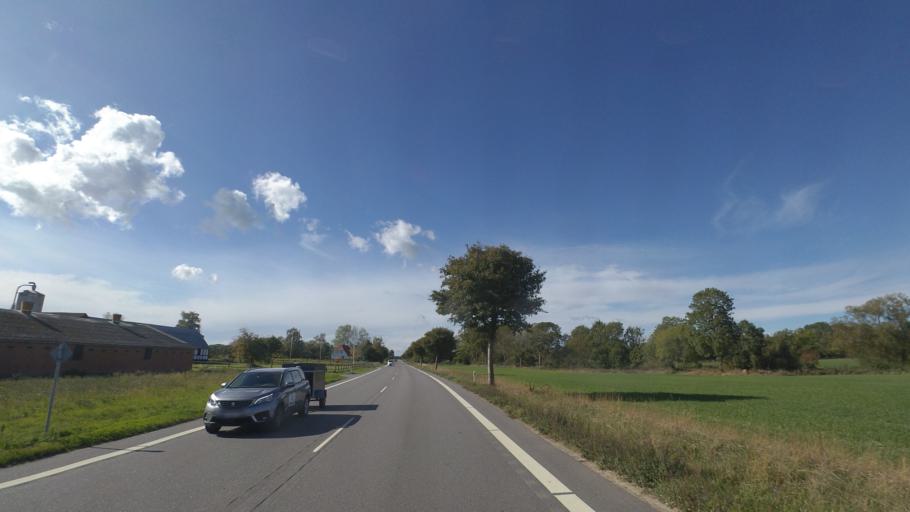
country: DK
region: Capital Region
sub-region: Bornholm Kommune
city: Ronne
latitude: 55.0743
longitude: 14.7932
